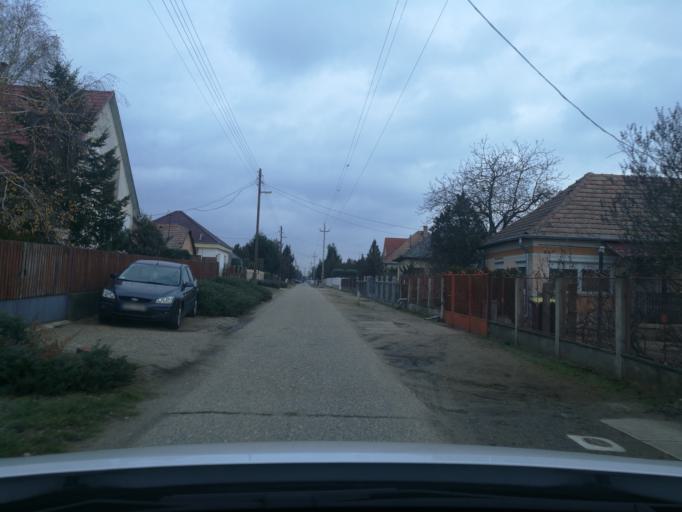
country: HU
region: Szabolcs-Szatmar-Bereg
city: Nyirpazony
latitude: 47.9753
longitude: 21.7946
